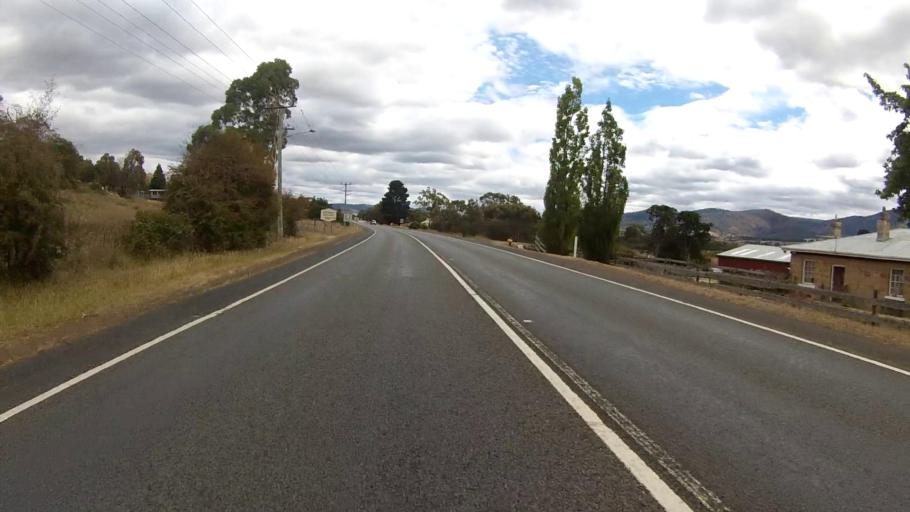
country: AU
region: Tasmania
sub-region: Brighton
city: Bridgewater
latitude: -42.6785
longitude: 147.2649
